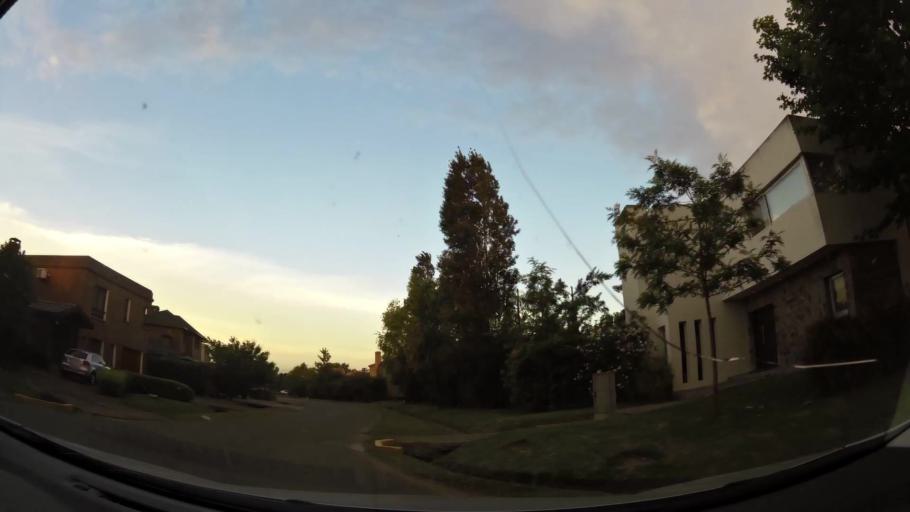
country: AR
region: Buenos Aires
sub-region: Partido de Tigre
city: Tigre
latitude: -34.4429
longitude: -58.6531
